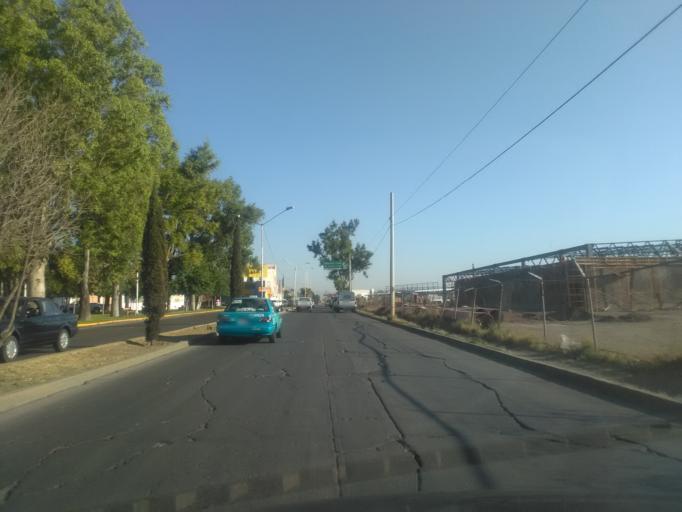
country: MX
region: Durango
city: Victoria de Durango
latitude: 24.0436
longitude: -104.6220
